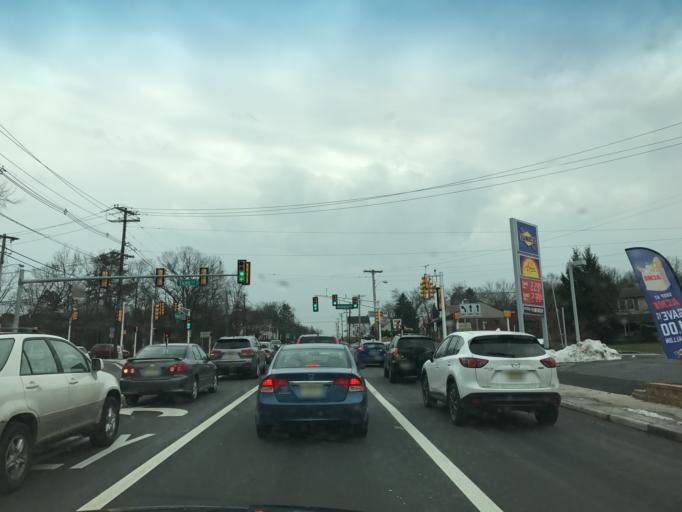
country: US
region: New Jersey
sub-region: Middlesex County
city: Milltown
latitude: 40.4562
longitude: -74.4249
